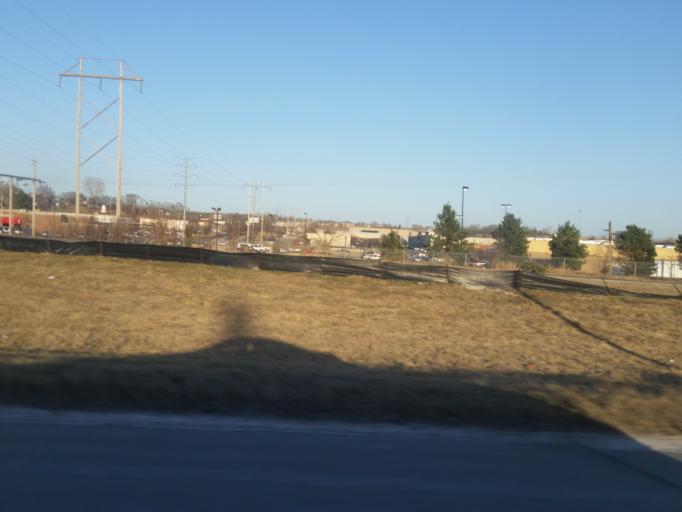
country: US
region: Nebraska
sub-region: Sarpy County
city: Offutt Air Force Base
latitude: 41.1569
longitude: -95.9387
